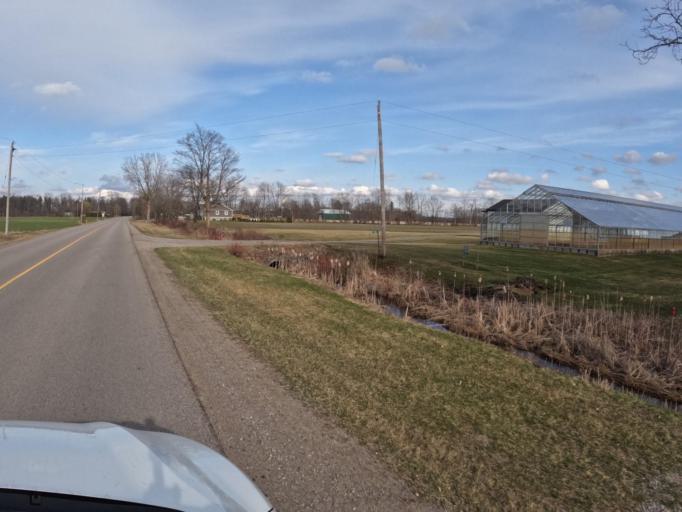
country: CA
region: Ontario
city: Brant
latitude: 43.0010
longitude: -80.4406
